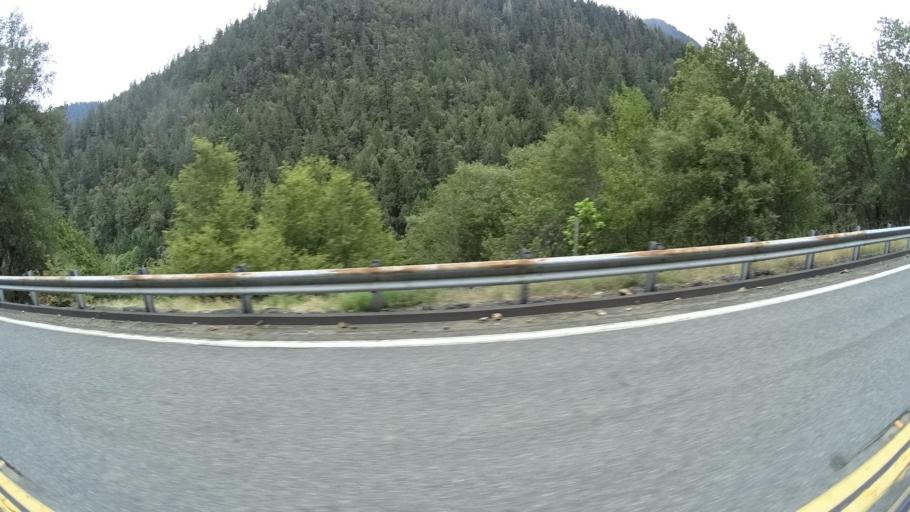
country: US
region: California
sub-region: Humboldt County
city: Willow Creek
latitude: 41.2598
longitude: -123.6107
